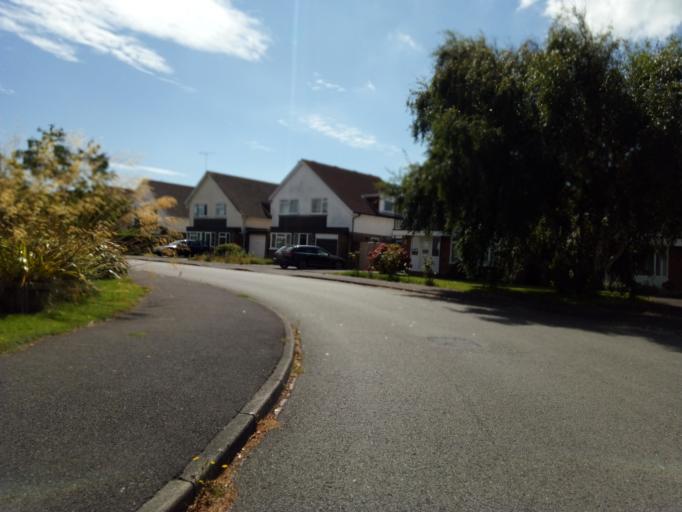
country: GB
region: England
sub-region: West Sussex
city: Barnham
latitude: 50.7914
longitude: -0.6327
